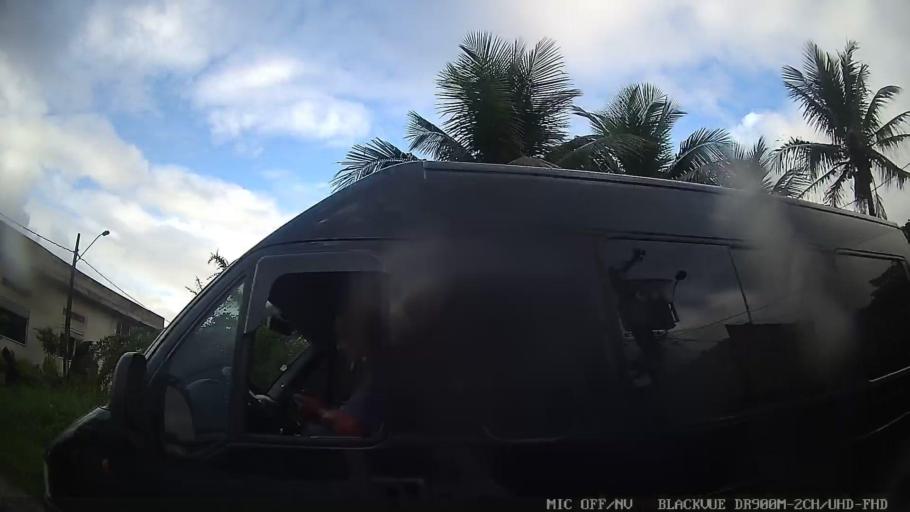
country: BR
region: Sao Paulo
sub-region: Itanhaem
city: Itanhaem
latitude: -24.2316
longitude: -46.9065
